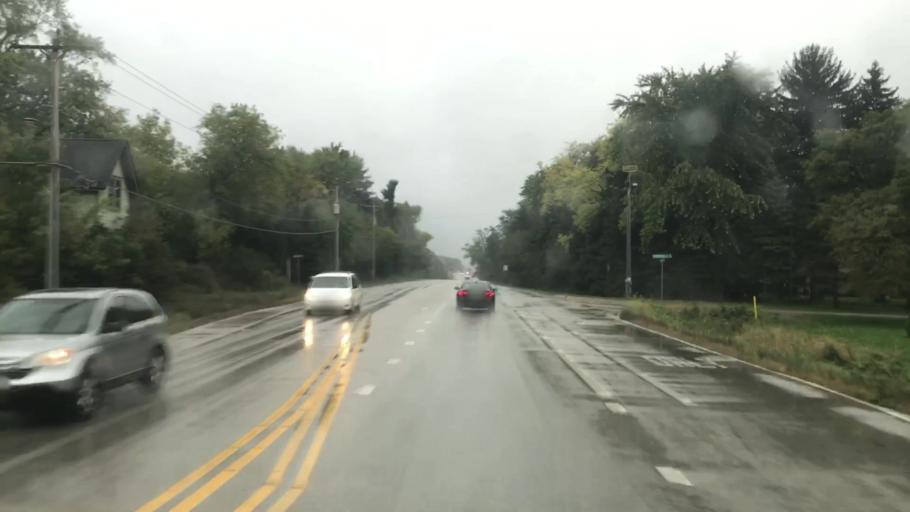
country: US
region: Wisconsin
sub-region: Ozaukee County
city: Mequon
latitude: 43.2295
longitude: -88.0036
